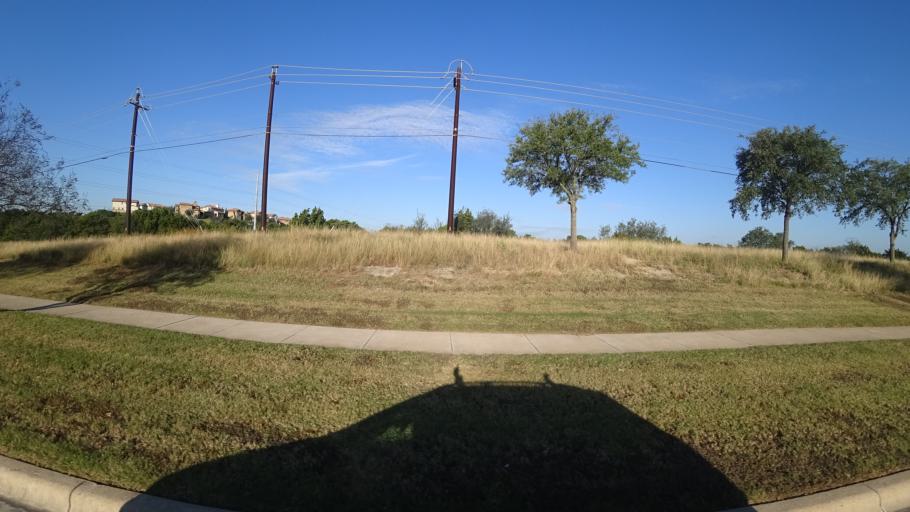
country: US
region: Texas
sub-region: Travis County
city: Hudson Bend
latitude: 30.3718
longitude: -97.8876
